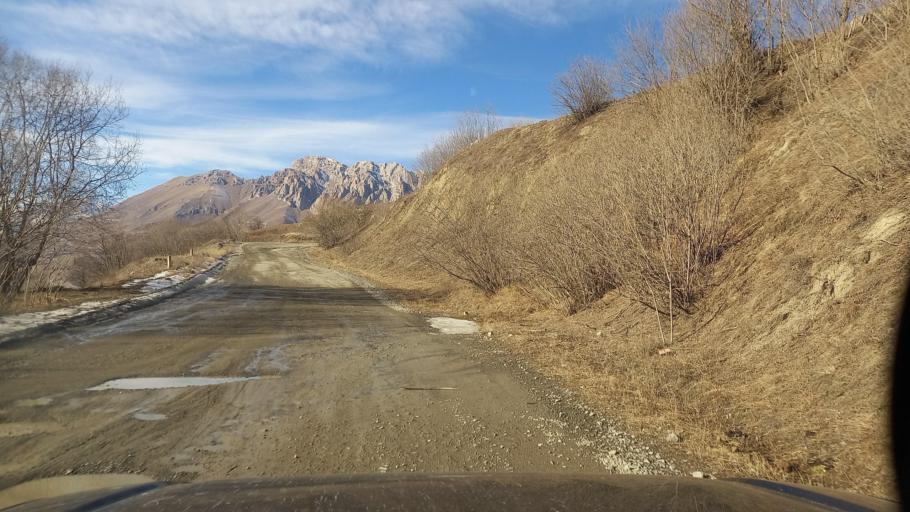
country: RU
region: North Ossetia
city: Verkhniy Fiagdon
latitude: 42.8365
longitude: 44.4722
